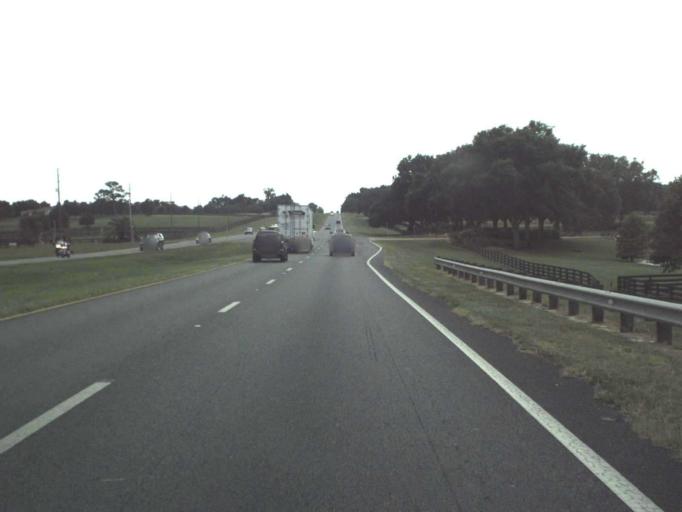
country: US
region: Florida
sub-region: Marion County
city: Citra
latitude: 29.3146
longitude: -82.1519
